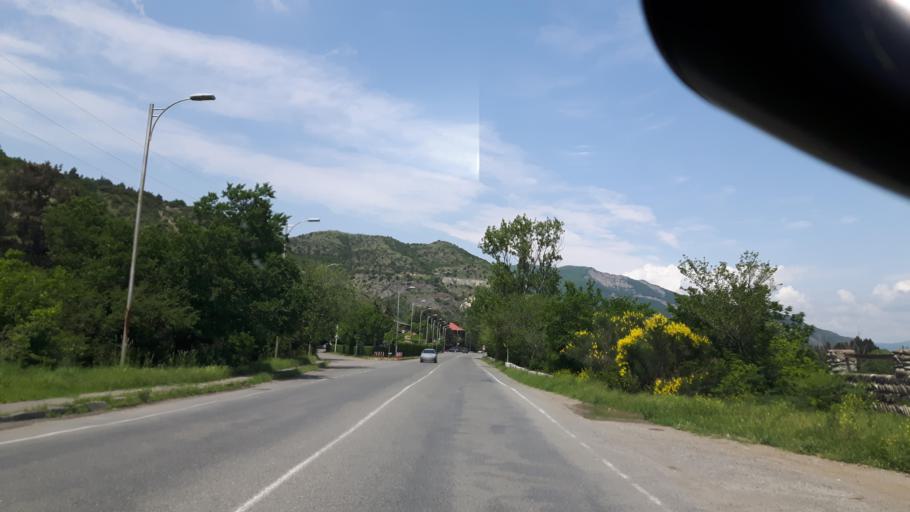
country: GE
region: Mtskheta-Mtianeti
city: Mtskheta
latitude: 41.8266
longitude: 44.7273
